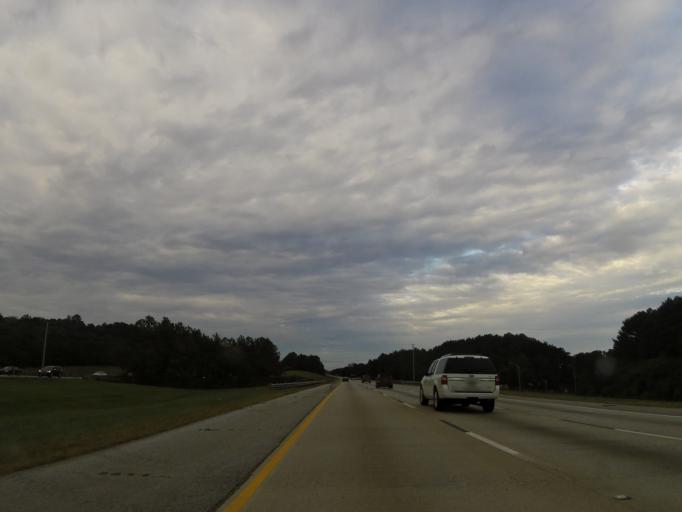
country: US
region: Alabama
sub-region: Jefferson County
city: Vestavia Hills
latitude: 33.4109
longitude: -86.7596
